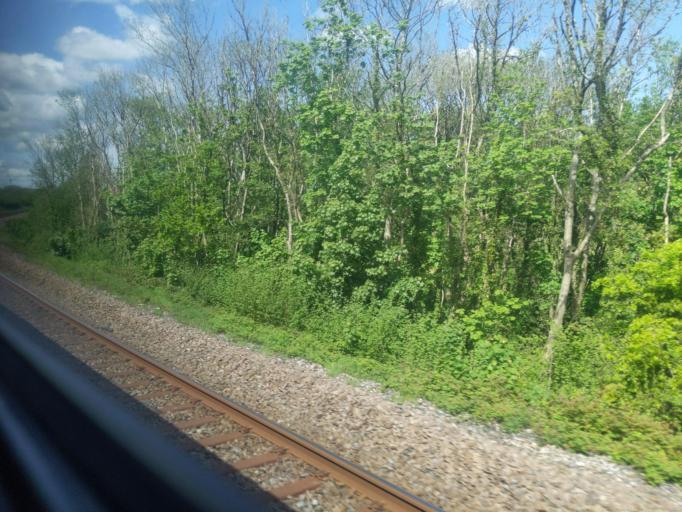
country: GB
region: England
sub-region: Cornwall
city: Pillaton
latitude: 50.4122
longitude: -4.3546
